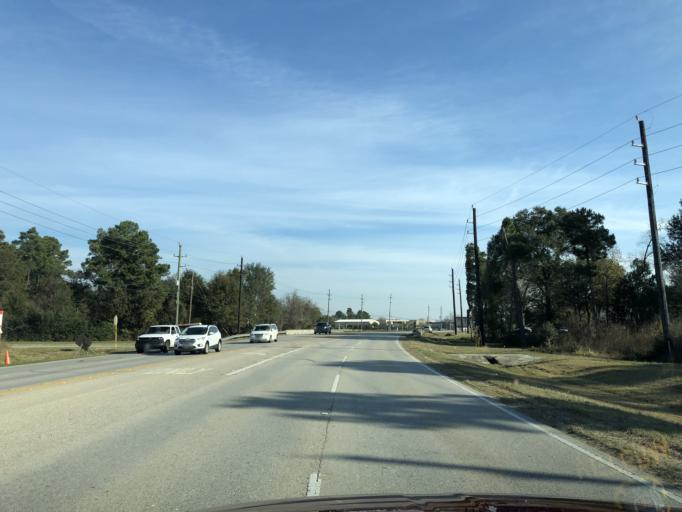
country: US
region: Texas
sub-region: Harris County
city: Tomball
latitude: 30.0416
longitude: -95.5456
